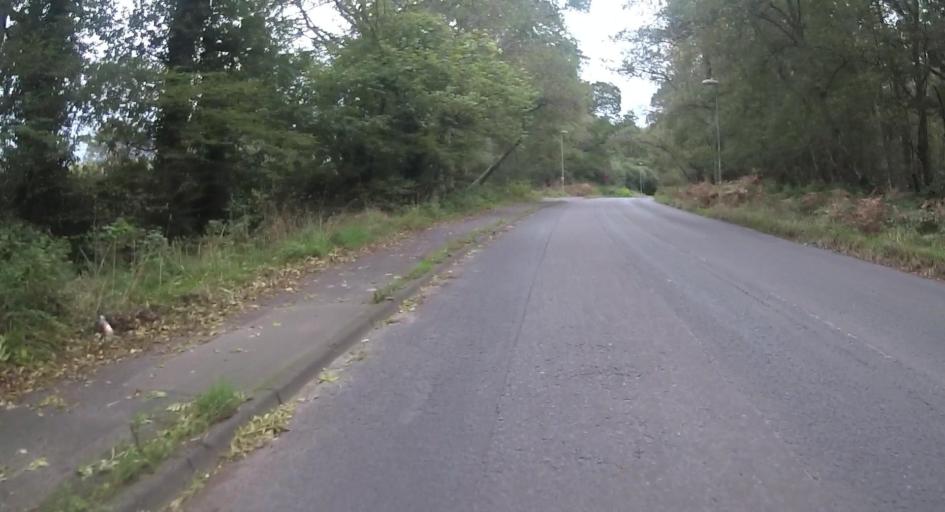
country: GB
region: England
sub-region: Hampshire
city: Fleet
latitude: 51.2767
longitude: -0.8635
